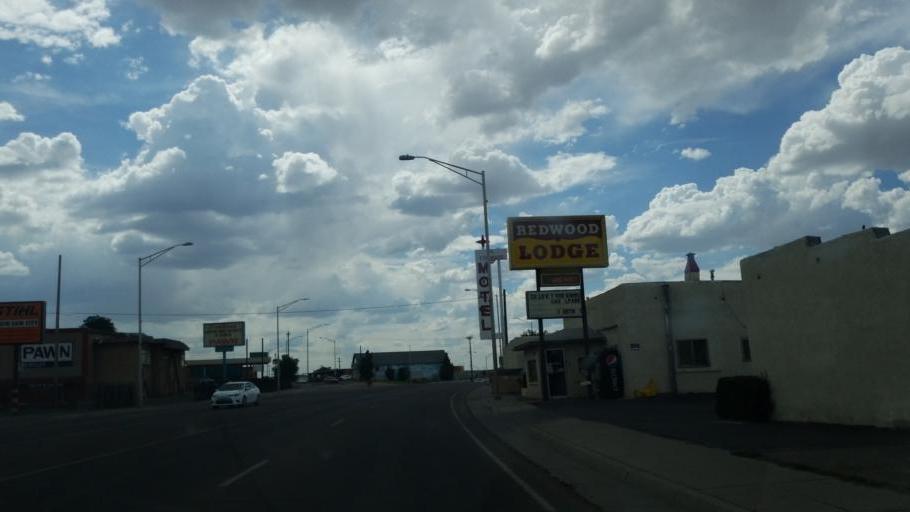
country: US
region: New Mexico
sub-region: McKinley County
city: Gallup
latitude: 35.5302
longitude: -108.7303
